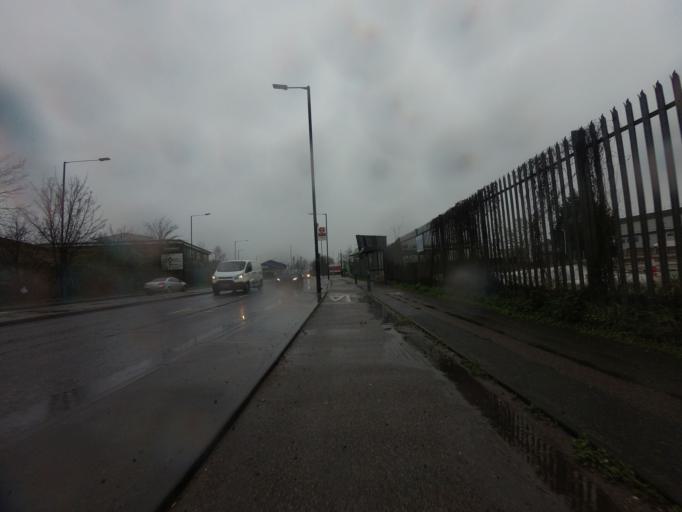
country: GB
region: England
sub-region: Hertfordshire
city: Waltham Cross
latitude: 51.6476
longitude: -0.0303
